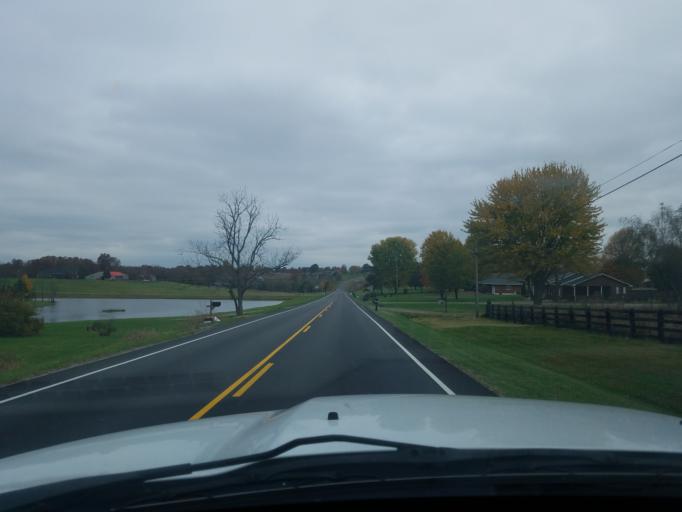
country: US
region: Kentucky
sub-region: Nelson County
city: Bardstown
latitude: 37.7763
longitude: -85.3750
